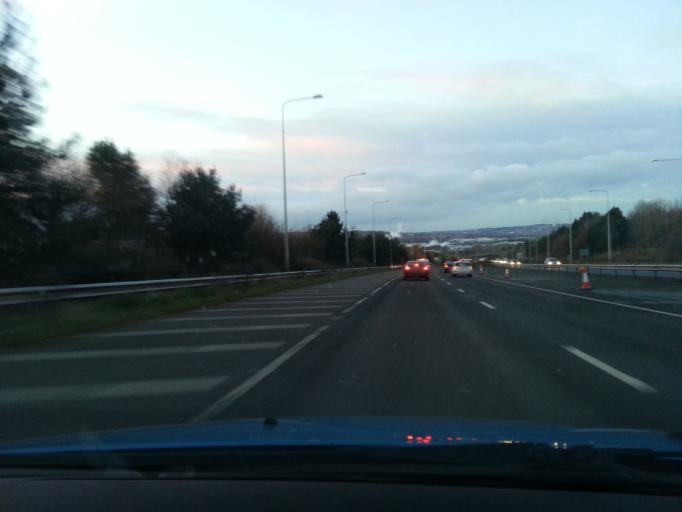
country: GB
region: England
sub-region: Gateshead
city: Lamesley
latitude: 54.9149
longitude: -1.5943
